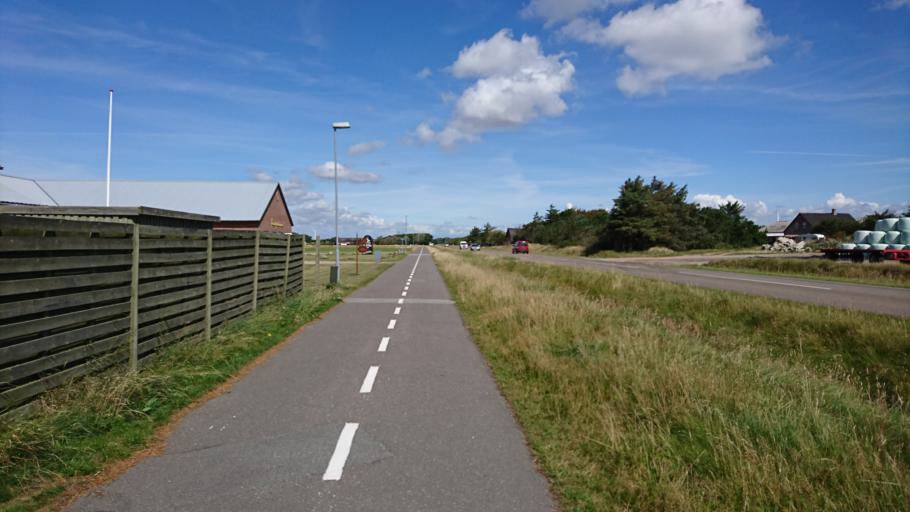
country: DK
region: South Denmark
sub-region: Fano Kommune
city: Nordby
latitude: 55.4204
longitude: 8.3983
